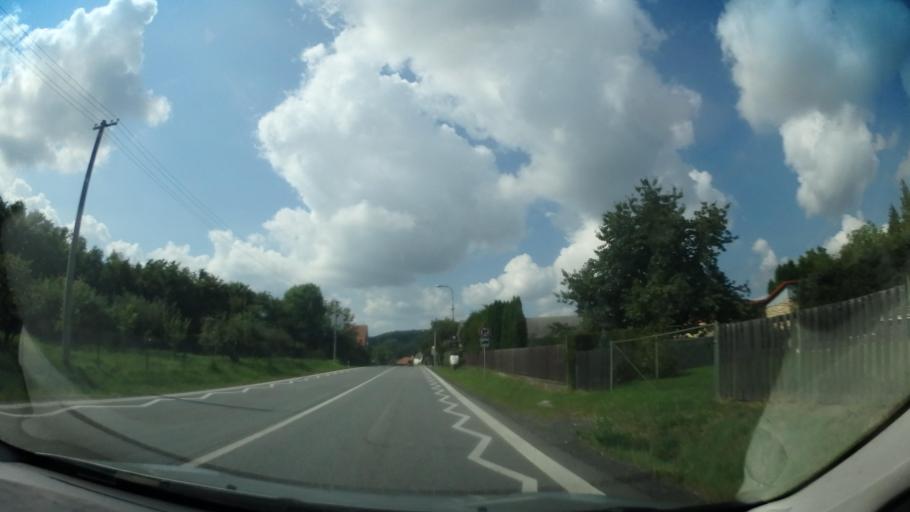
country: CZ
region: Central Bohemia
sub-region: Okres Kolin
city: Kourim
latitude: 49.9671
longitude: 14.9589
